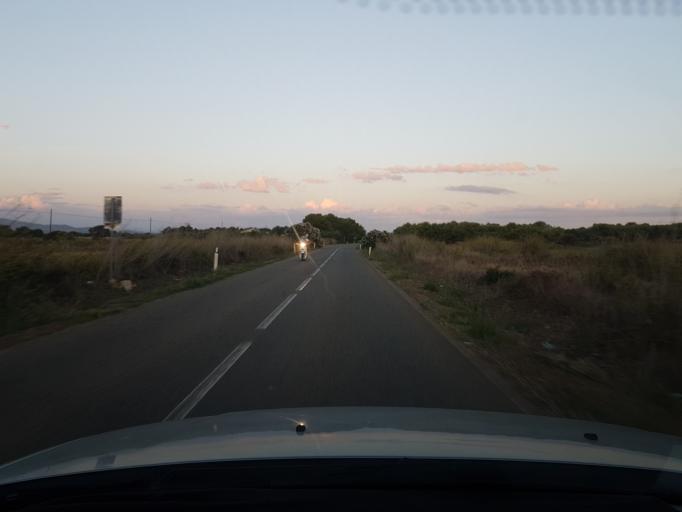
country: IT
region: Sardinia
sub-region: Provincia di Oristano
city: Riola Sardo
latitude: 40.0282
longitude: 8.4240
